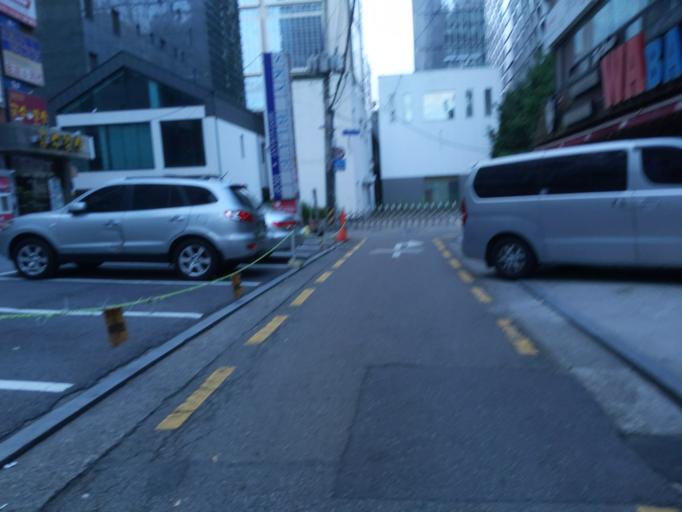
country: KR
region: Seoul
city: Seoul
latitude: 37.5084
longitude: 127.0583
